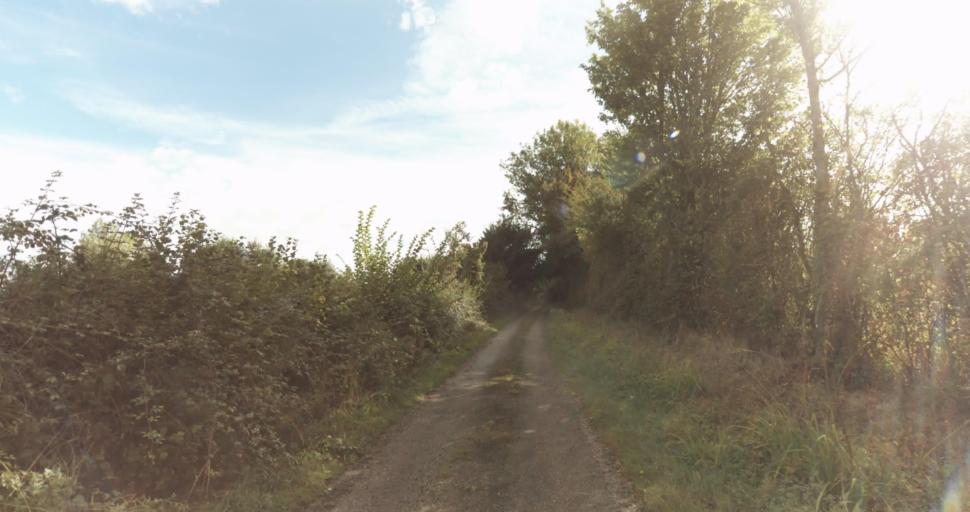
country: FR
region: Lower Normandy
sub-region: Departement de l'Orne
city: Vimoutiers
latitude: 48.8824
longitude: 0.1759
